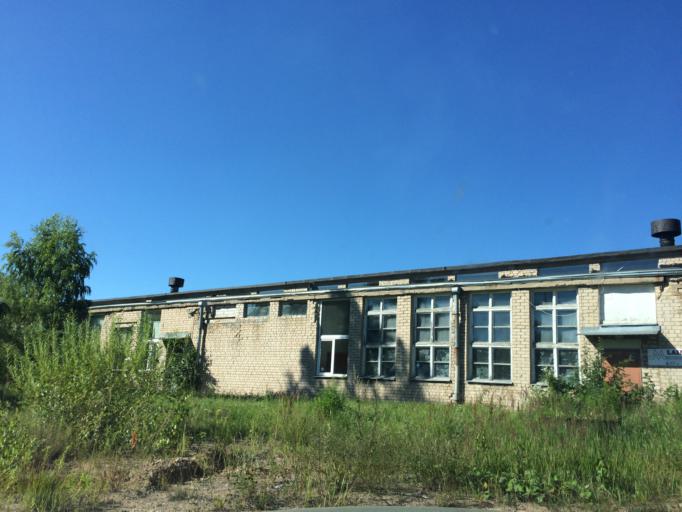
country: LV
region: Rezekne
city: Rezekne
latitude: 56.5276
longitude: 27.3385
